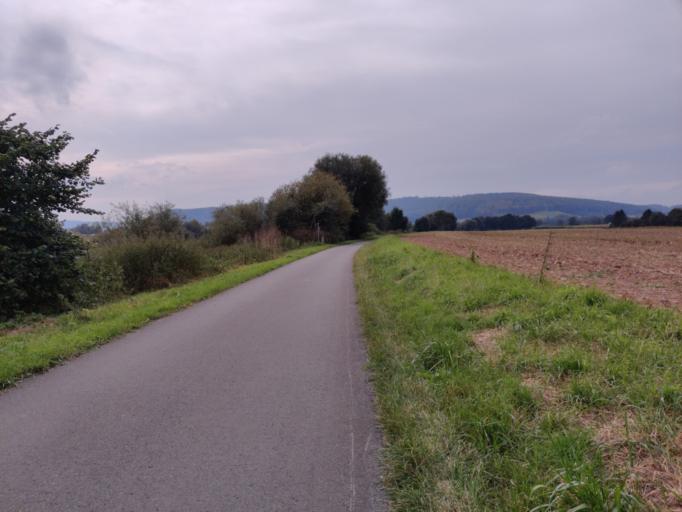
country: DE
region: Lower Saxony
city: Holzminden
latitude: 51.8184
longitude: 9.4303
